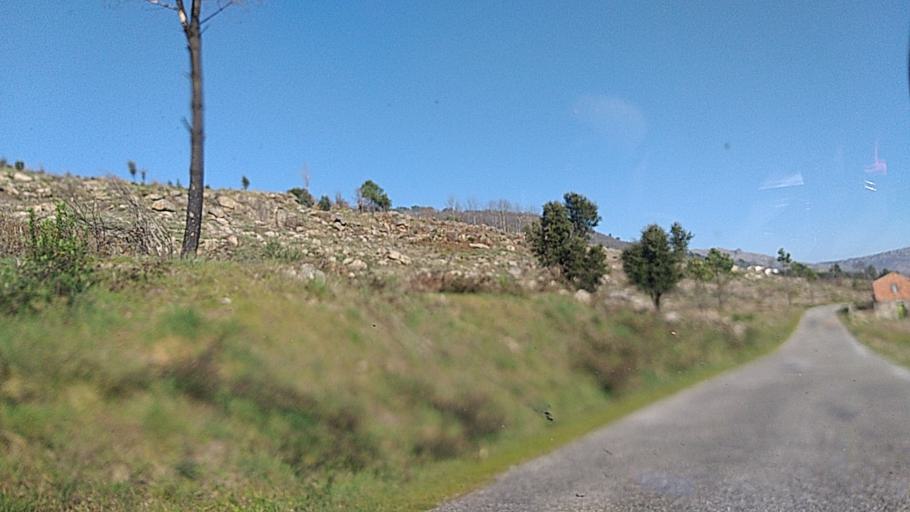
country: PT
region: Guarda
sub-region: Celorico da Beira
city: Celorico da Beira
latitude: 40.6730
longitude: -7.4566
